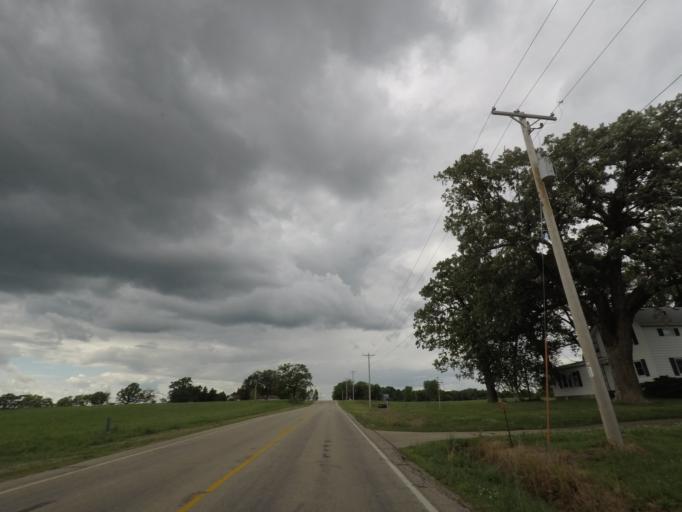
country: US
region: Wisconsin
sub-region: Green County
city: Brooklyn
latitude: 42.8410
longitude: -89.4125
